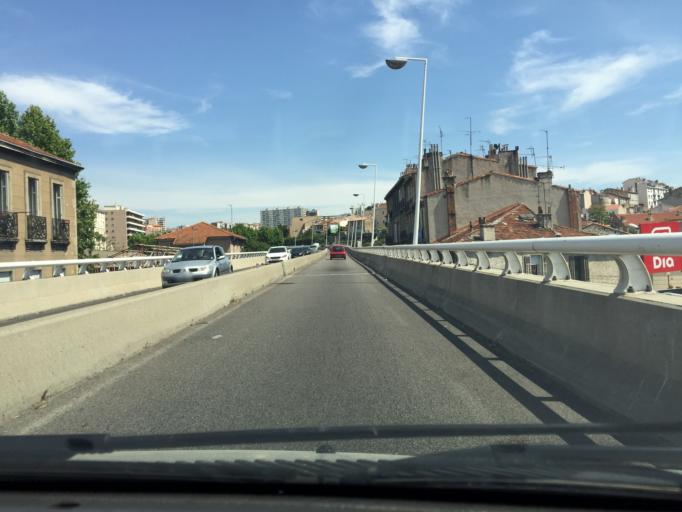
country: FR
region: Provence-Alpes-Cote d'Azur
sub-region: Departement des Bouches-du-Rhone
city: Marseille 03
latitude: 43.3155
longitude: 5.3860
